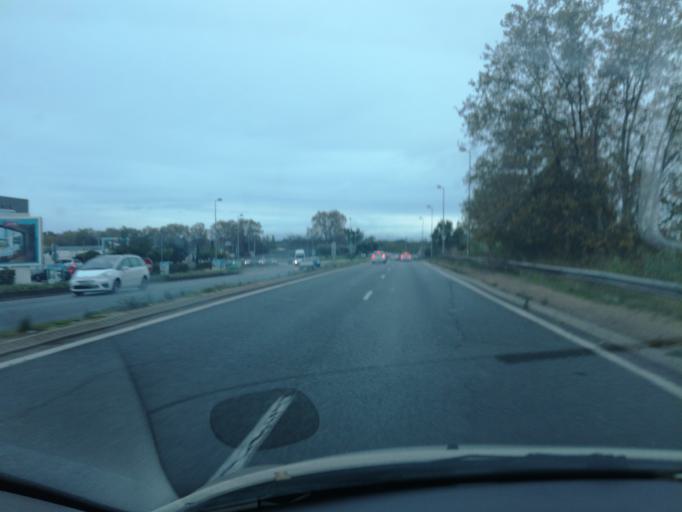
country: FR
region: Provence-Alpes-Cote d'Azur
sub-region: Departement du Var
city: Puget-sur-Argens
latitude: 43.4407
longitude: 6.7061
